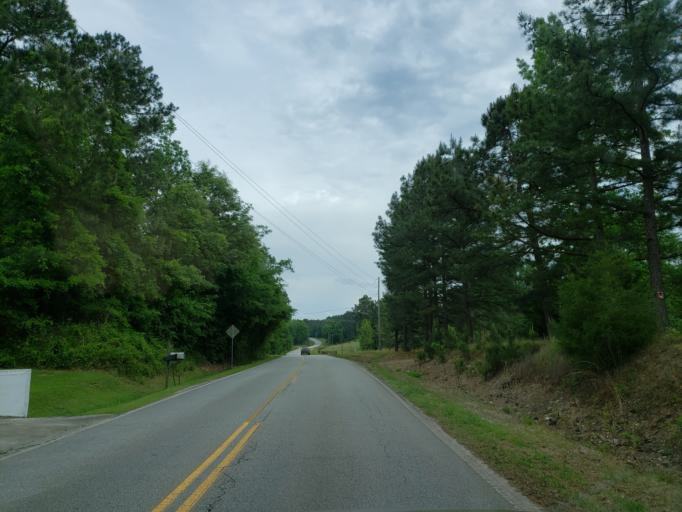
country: US
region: Georgia
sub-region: Bibb County
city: West Point
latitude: 32.8193
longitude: -83.8610
